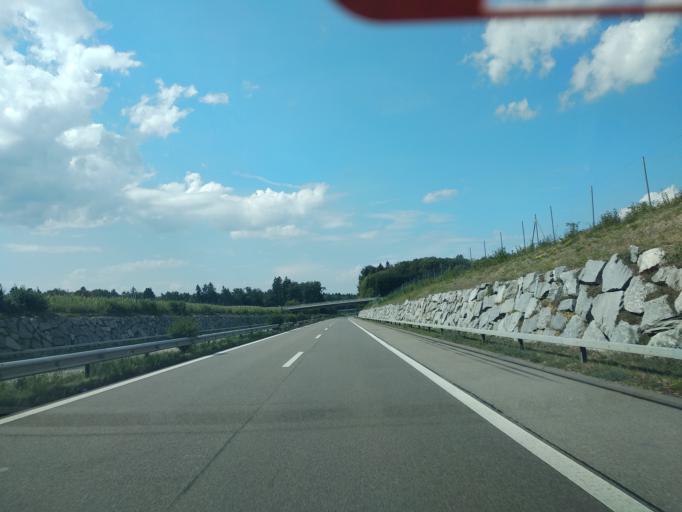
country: CH
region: Thurgau
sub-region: Kreuzlingen District
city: Tagerwilen
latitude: 47.6197
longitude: 9.1130
